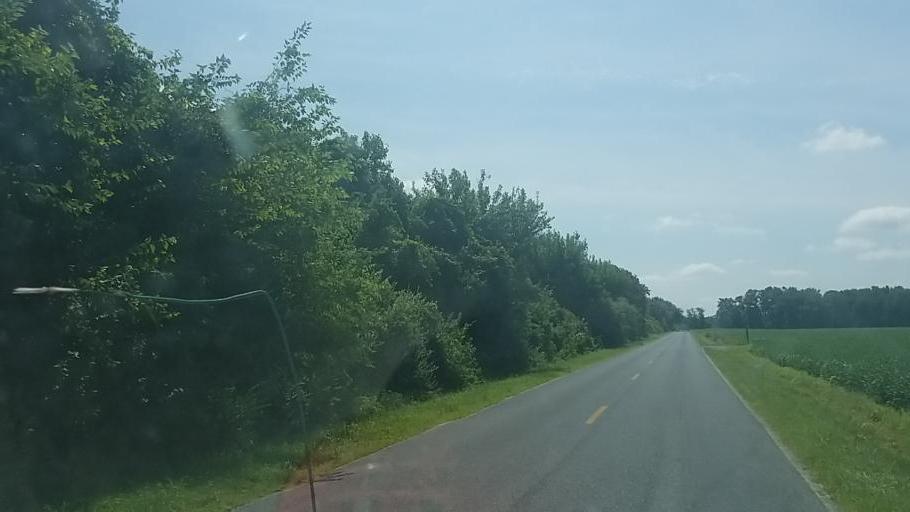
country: US
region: Maryland
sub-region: Caroline County
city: Ridgely
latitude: 38.9063
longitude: -75.9346
